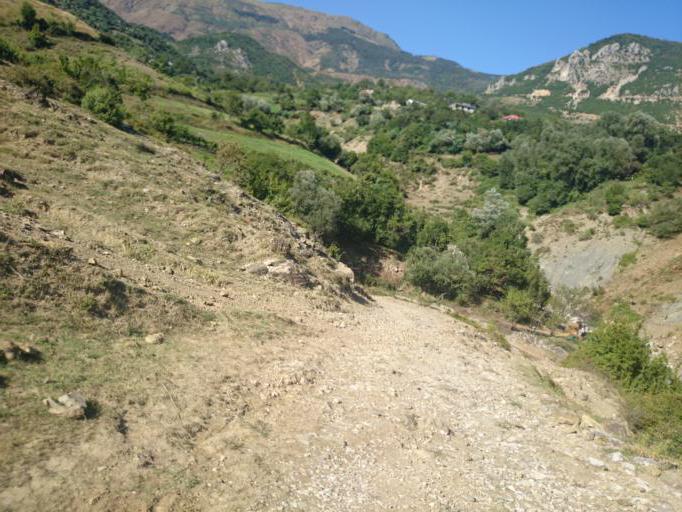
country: AL
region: Elbasan
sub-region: Rrethi i Gramshit
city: Kukur
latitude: 40.8661
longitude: 20.3556
